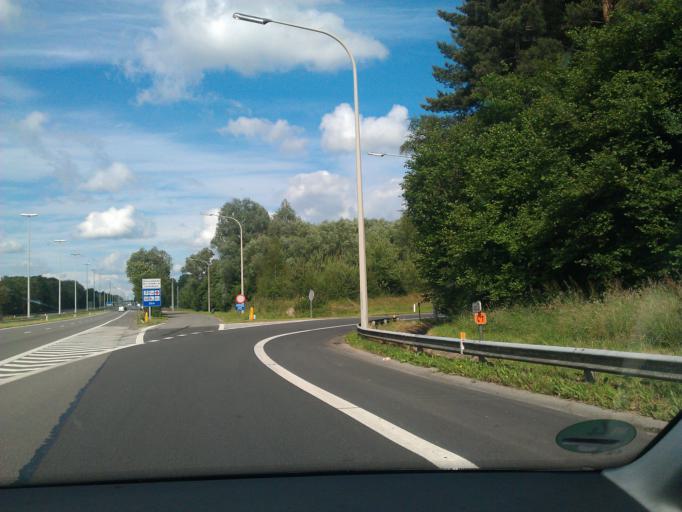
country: BE
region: Wallonia
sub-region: Province de Liege
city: Raeren
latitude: 50.7030
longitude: 6.0879
